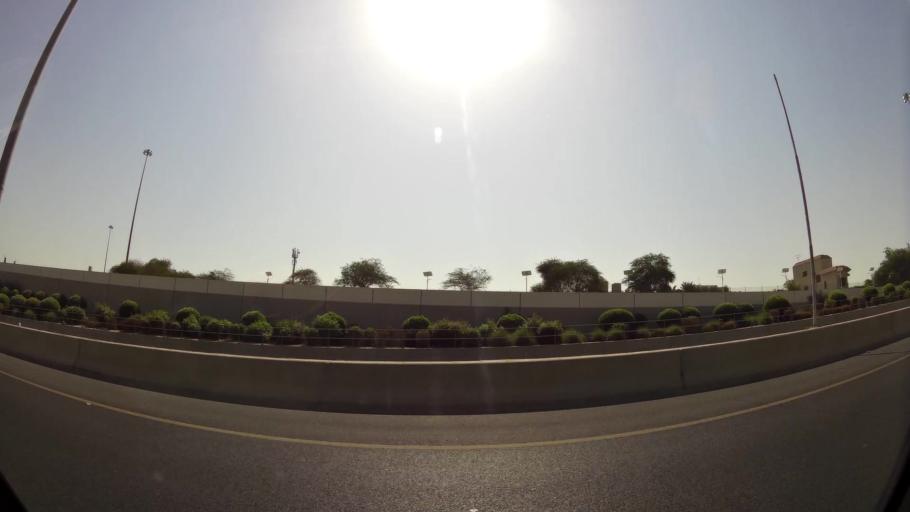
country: KW
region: Al Asimah
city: Kuwait City
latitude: 29.3606
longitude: 47.9856
